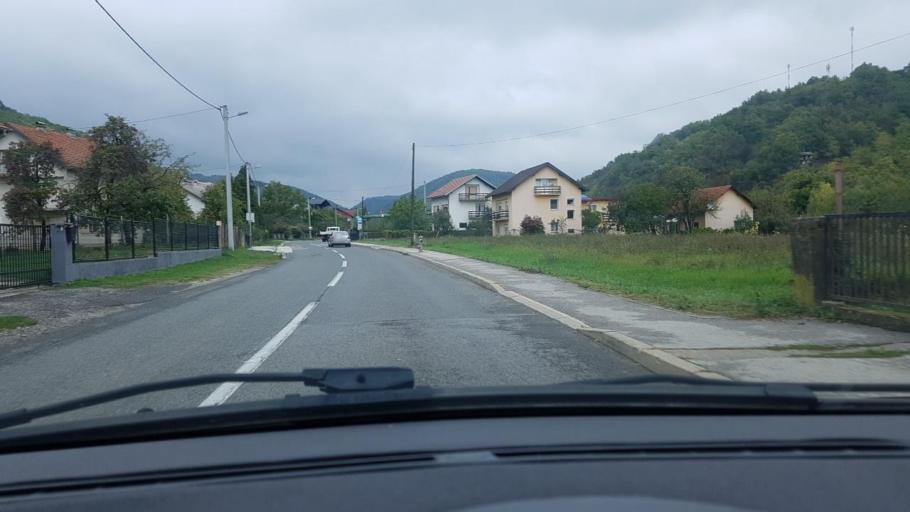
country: HR
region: Grad Zagreb
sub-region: Sesvete
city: Sesvete
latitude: 45.9143
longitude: 16.1241
